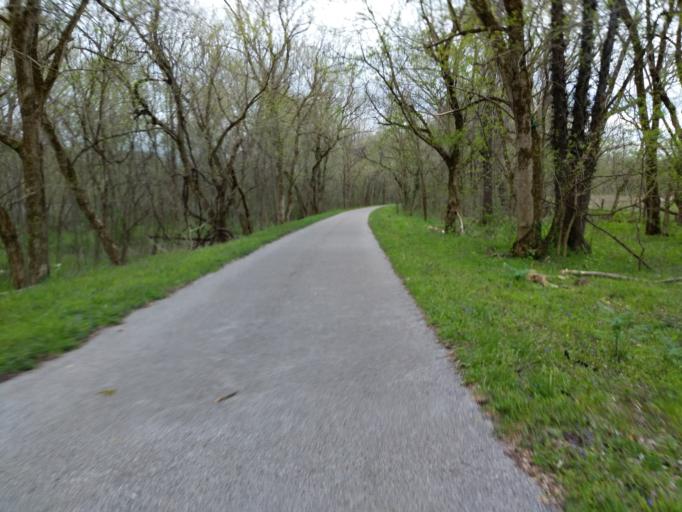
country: US
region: Ohio
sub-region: Athens County
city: Chauncey
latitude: 39.3836
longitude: -82.1164
